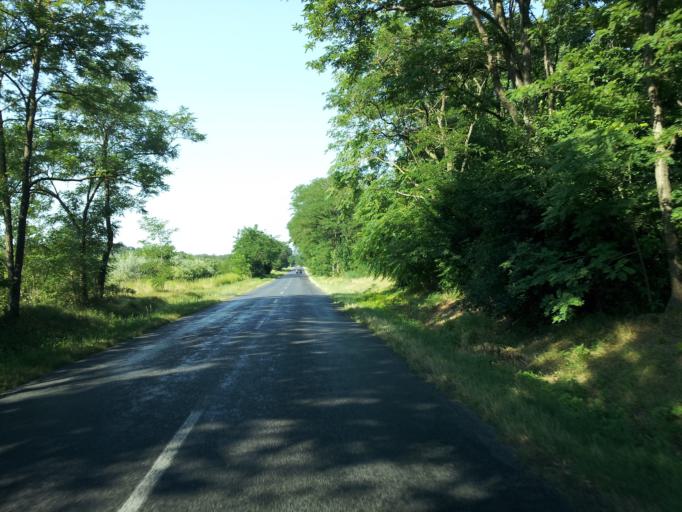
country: HU
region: Zala
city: Cserszegtomaj
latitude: 46.8677
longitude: 17.2086
